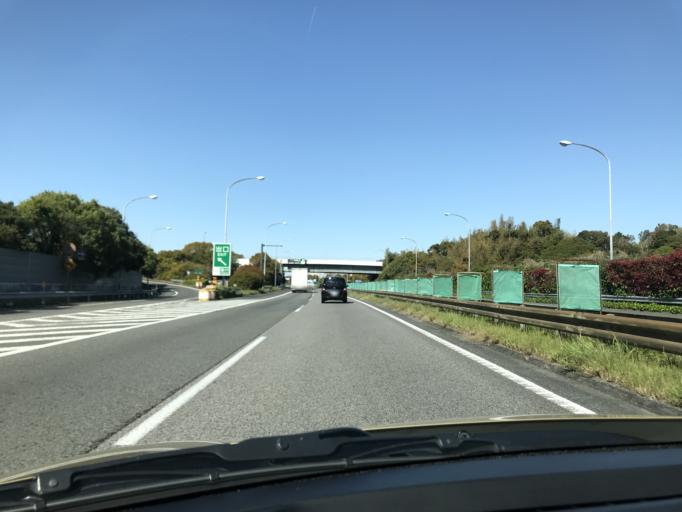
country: JP
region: Shizuoka
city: Kakegawa
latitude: 34.7652
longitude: 138.0264
